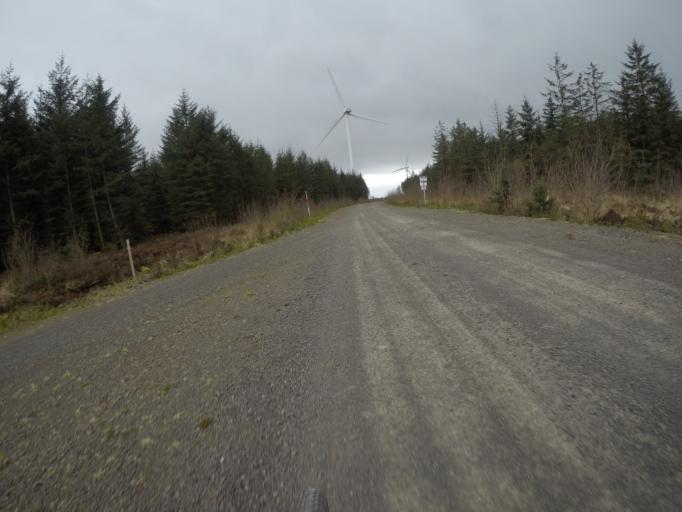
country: GB
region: Scotland
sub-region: East Ayrshire
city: Newmilns
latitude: 55.6768
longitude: -4.3350
